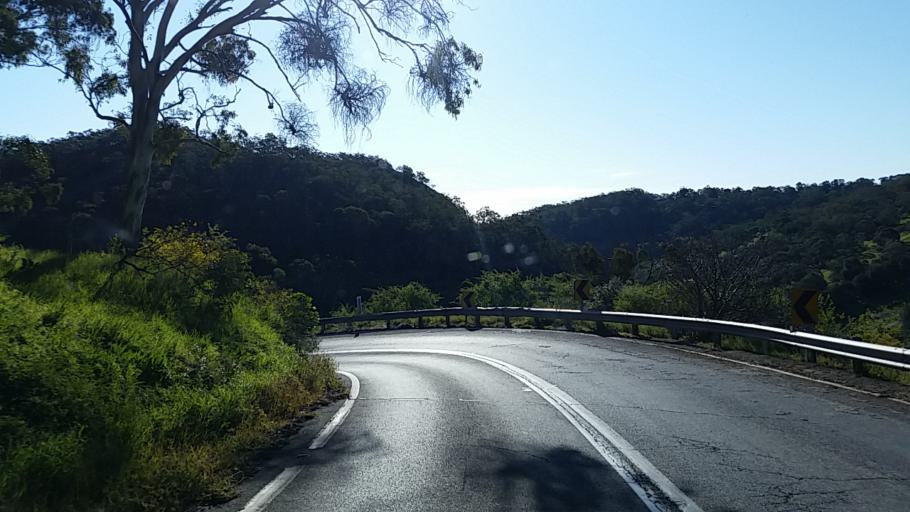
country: AU
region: South Australia
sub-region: Adelaide Hills
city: Adelaide Hills
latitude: -34.9242
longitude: 138.7201
